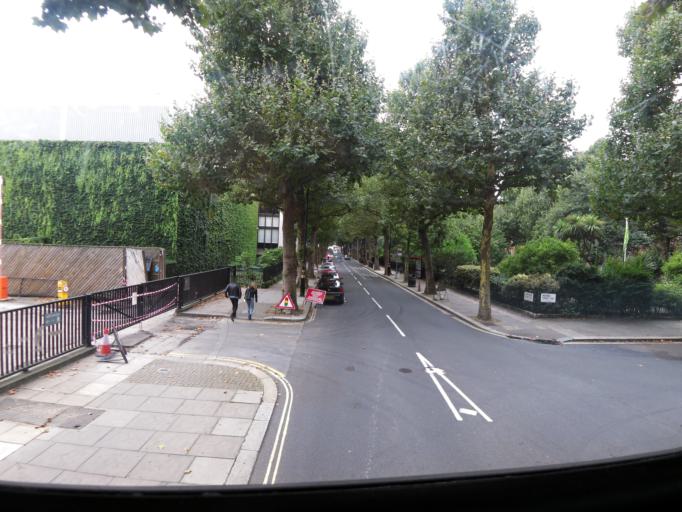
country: GB
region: England
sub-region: Greater London
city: City of Westminster
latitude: 51.4920
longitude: -0.1284
